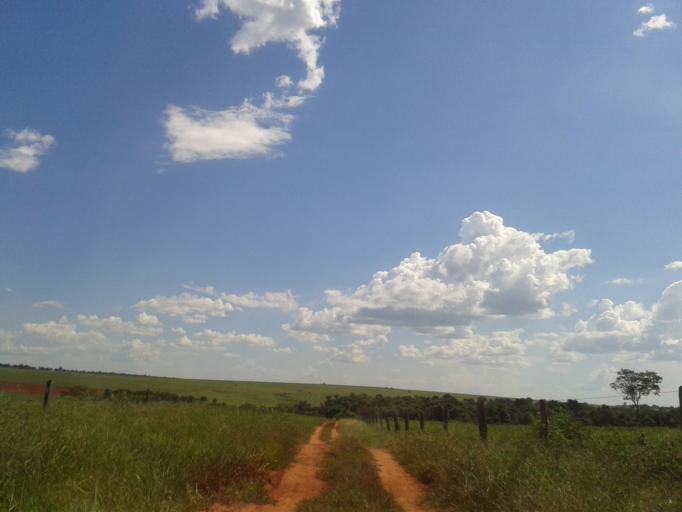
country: BR
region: Minas Gerais
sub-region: Santa Vitoria
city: Santa Vitoria
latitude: -19.1151
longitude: -50.4998
